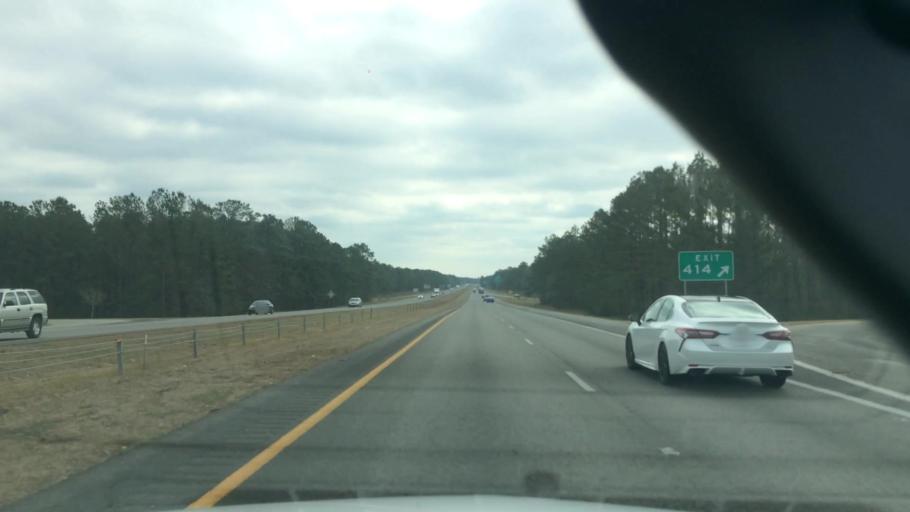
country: US
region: North Carolina
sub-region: New Hanover County
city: Castle Hayne
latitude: 34.3522
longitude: -77.8847
